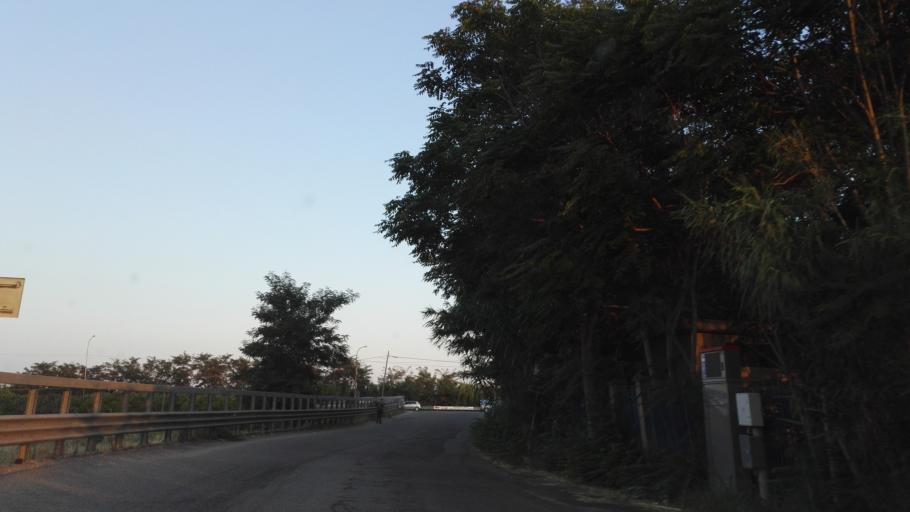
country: IT
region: Calabria
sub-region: Provincia di Reggio Calabria
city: Caulonia Marina
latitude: 38.3504
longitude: 16.4744
